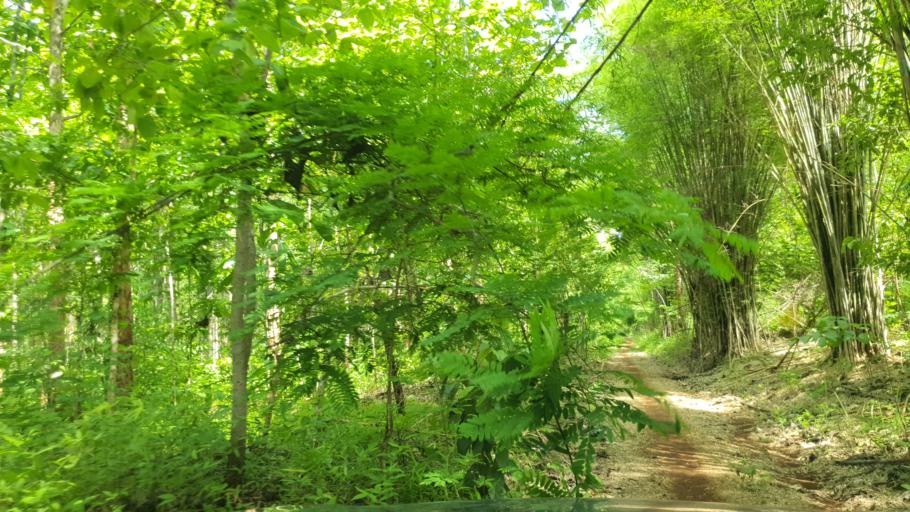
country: TH
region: Chiang Mai
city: Mae Taeng
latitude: 19.0767
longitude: 99.0973
